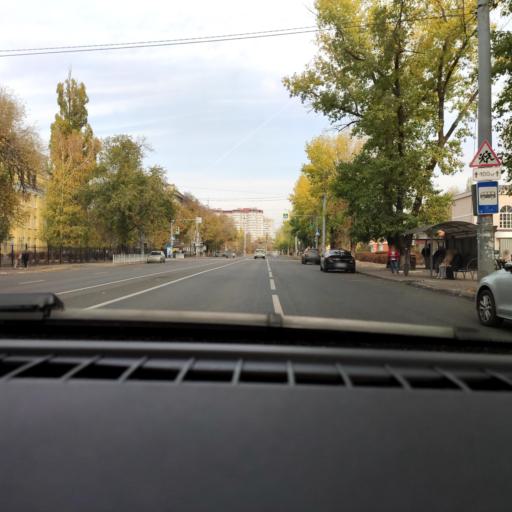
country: RU
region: Voronezj
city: Maslovka
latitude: 51.6119
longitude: 39.2462
